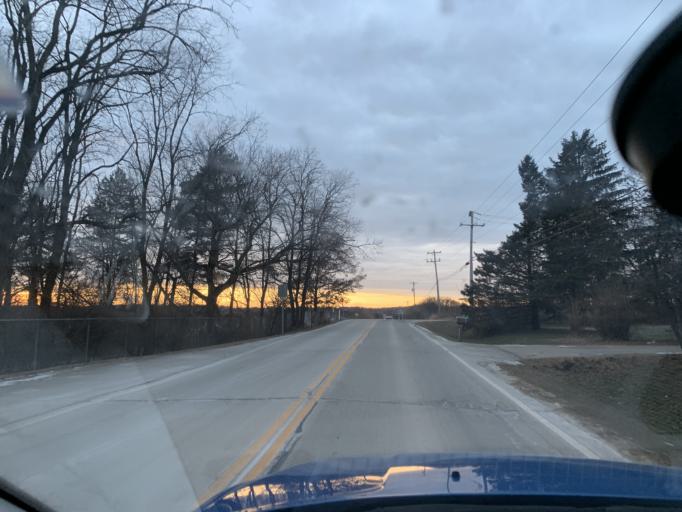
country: US
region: Wisconsin
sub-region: Dane County
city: Verona
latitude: 43.0457
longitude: -89.5514
